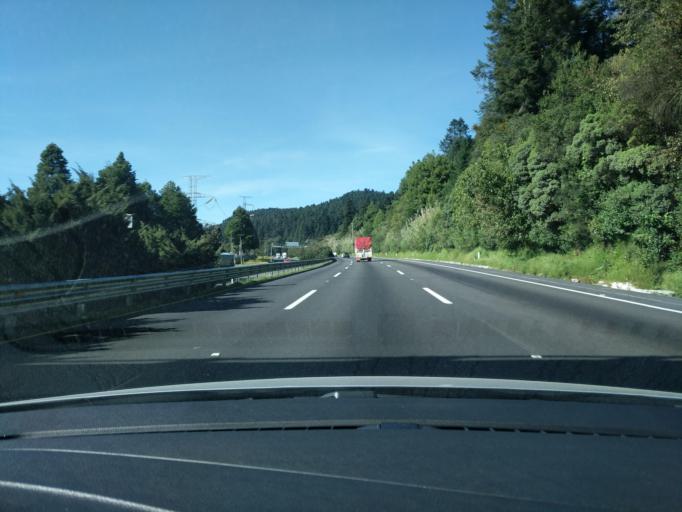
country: MX
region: Mexico City
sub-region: Cuajimalpa de Morelos
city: San Lorenzo Acopilco
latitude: 19.3096
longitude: -99.3430
